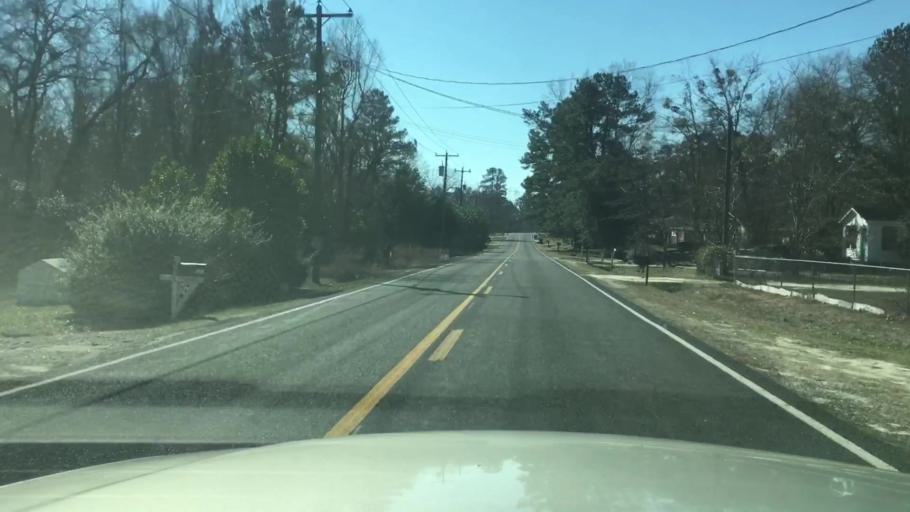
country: US
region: North Carolina
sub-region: Cumberland County
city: Hope Mills
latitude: 35.0011
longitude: -78.9646
